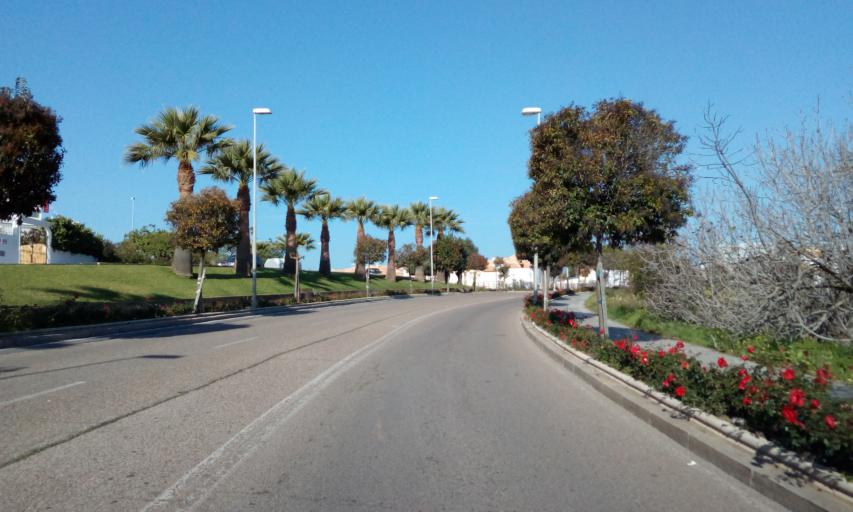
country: ES
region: Andalusia
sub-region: Provincia de Huelva
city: Ayamonte
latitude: 37.2214
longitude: -7.4007
